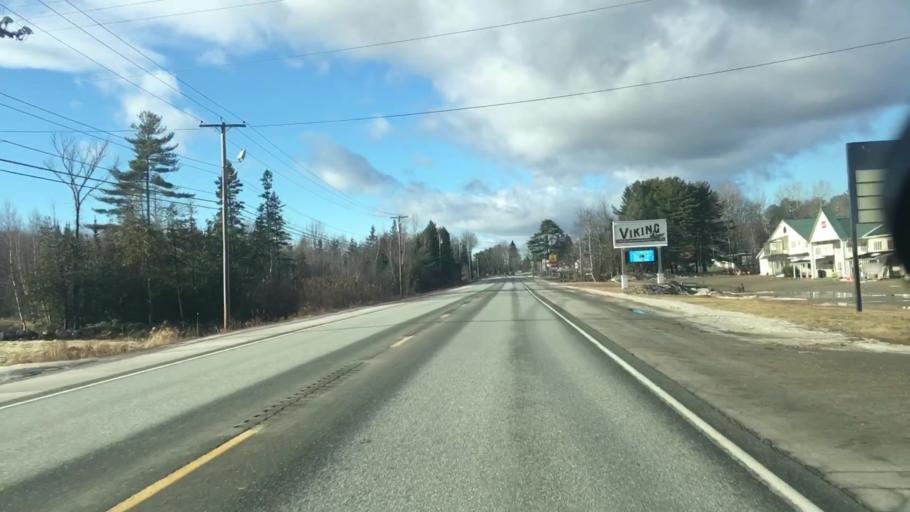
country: US
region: Maine
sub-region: Penobscot County
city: Holden
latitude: 44.7531
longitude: -68.6570
